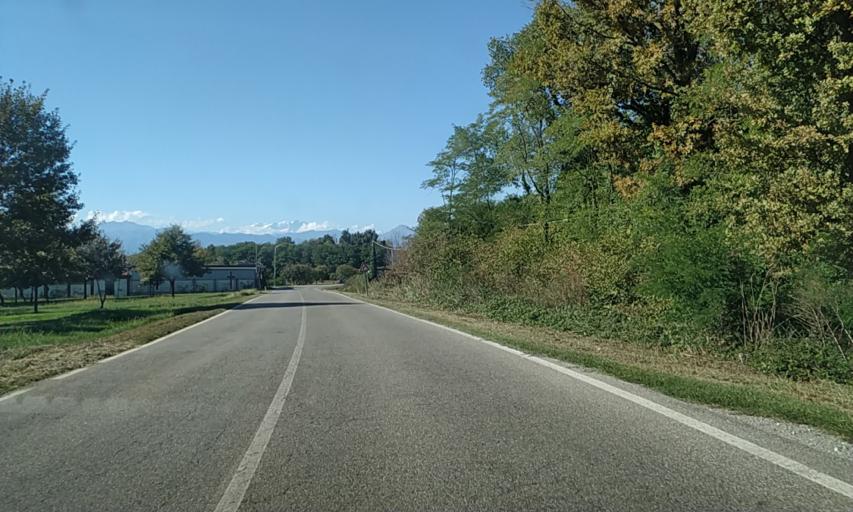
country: IT
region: Piedmont
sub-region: Provincia di Vercelli
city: Rovasenda
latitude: 45.5299
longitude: 8.3169
